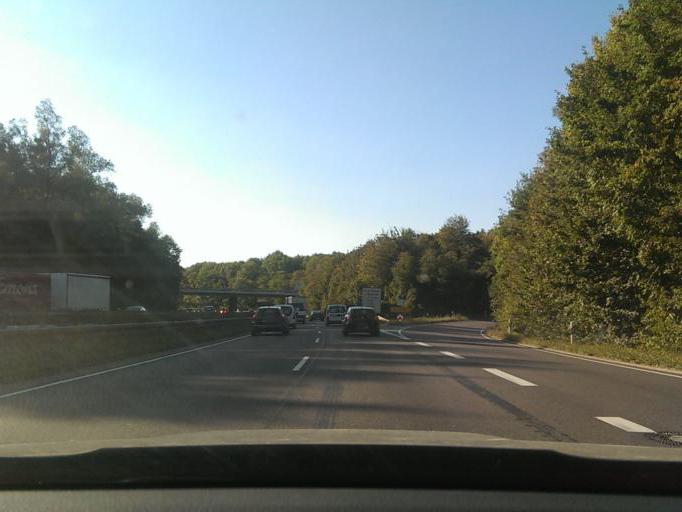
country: DE
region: Baden-Wuerttemberg
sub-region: Karlsruhe Region
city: Karlsruhe
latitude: 48.9942
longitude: 8.4291
